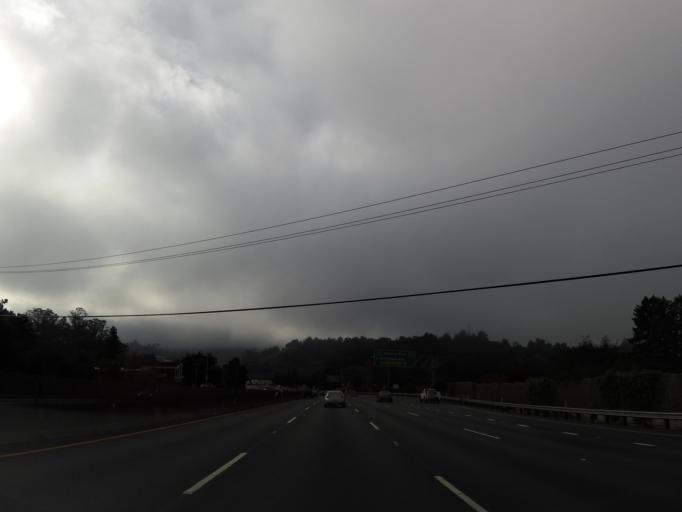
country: US
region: California
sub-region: Marin County
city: Strawberry
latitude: 37.9076
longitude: -122.5146
